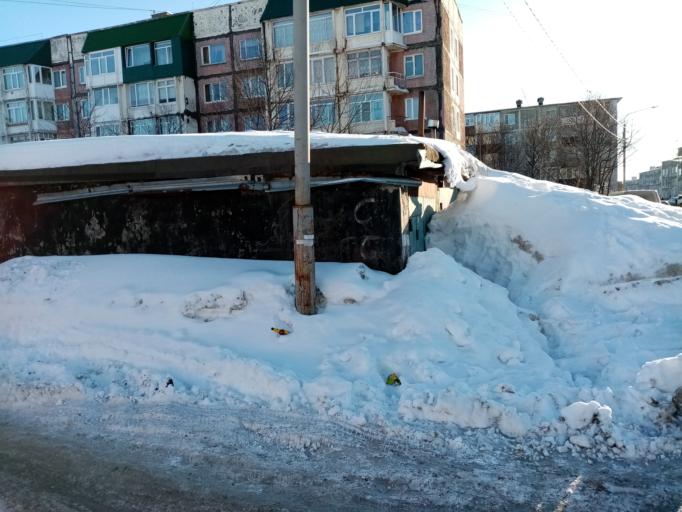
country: RU
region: Kamtsjatka
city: Petropavlovsk-Kamchatsky
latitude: 53.0696
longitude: 158.5945
